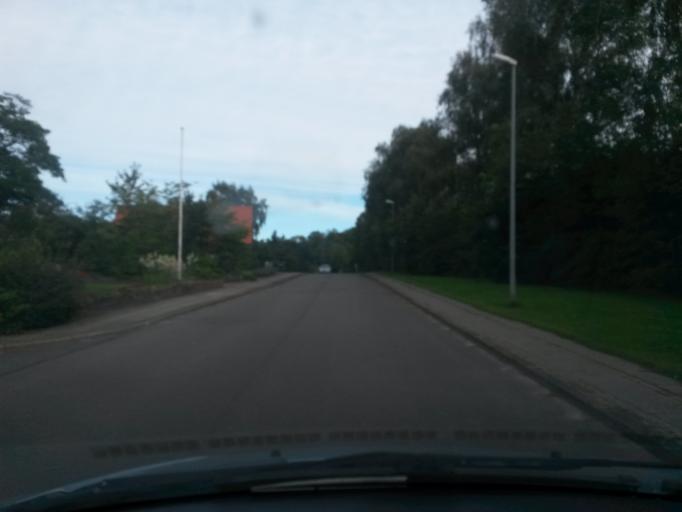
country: DK
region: Central Jutland
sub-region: Silkeborg Kommune
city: Kjellerup
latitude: 56.2893
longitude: 9.4406
